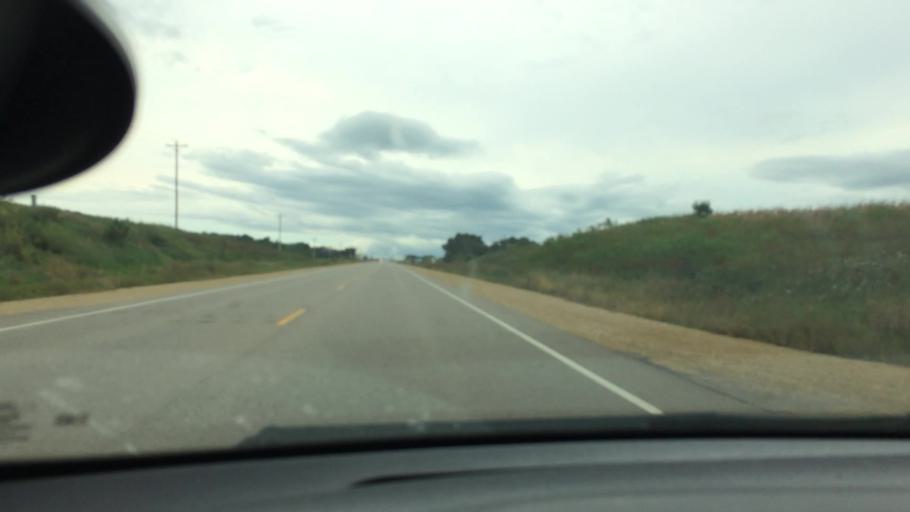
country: US
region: Wisconsin
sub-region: Trempealeau County
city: Osseo
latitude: 44.5875
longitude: -91.1828
